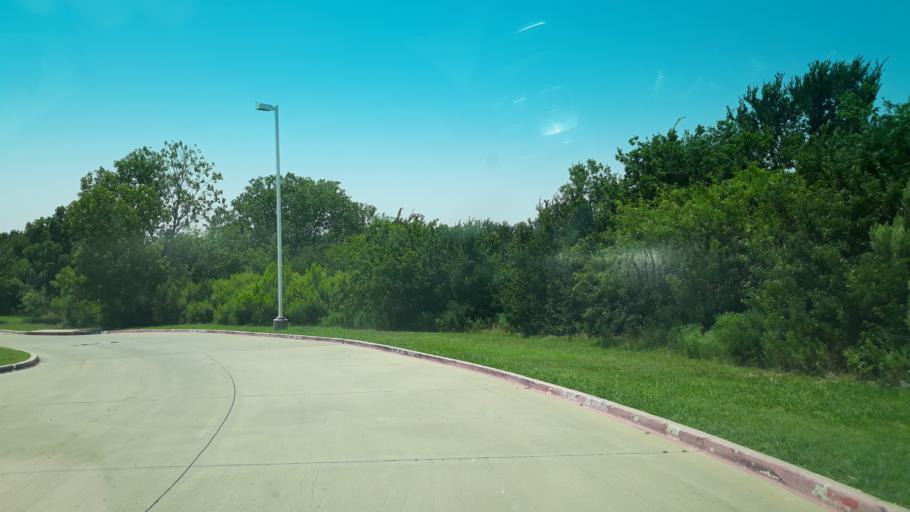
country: US
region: Texas
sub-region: Dallas County
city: Irving
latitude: 32.8691
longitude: -96.9631
